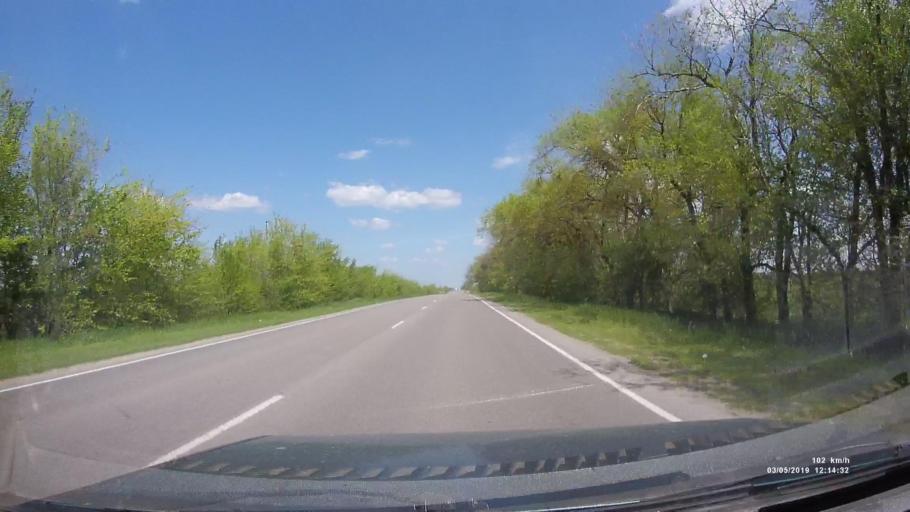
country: RU
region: Rostov
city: Melikhovskaya
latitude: 47.3453
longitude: 40.5643
